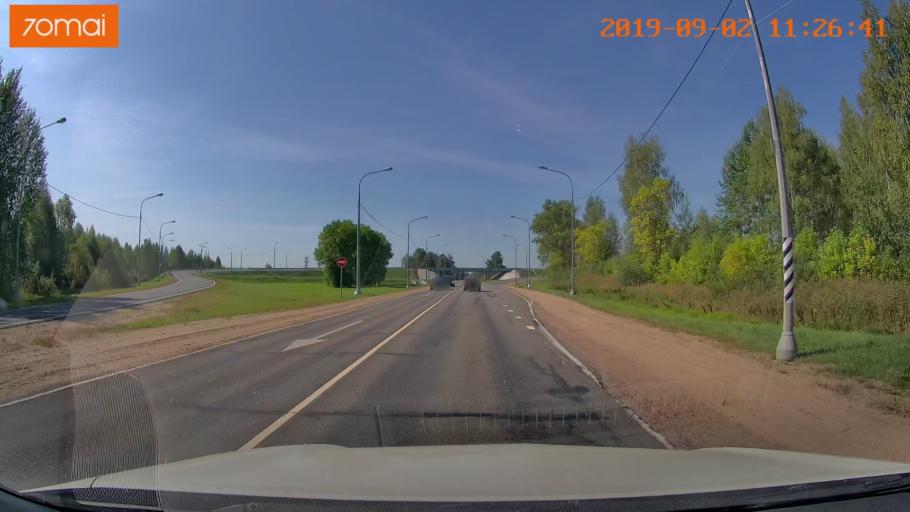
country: RU
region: Smolensk
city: Roslavl'
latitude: 53.9910
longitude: 32.9275
